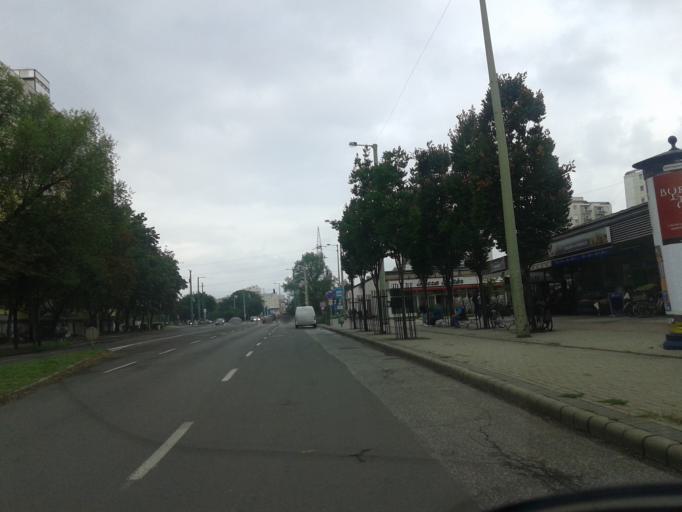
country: HU
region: Csongrad
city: Szeged
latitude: 46.2723
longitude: 20.1611
